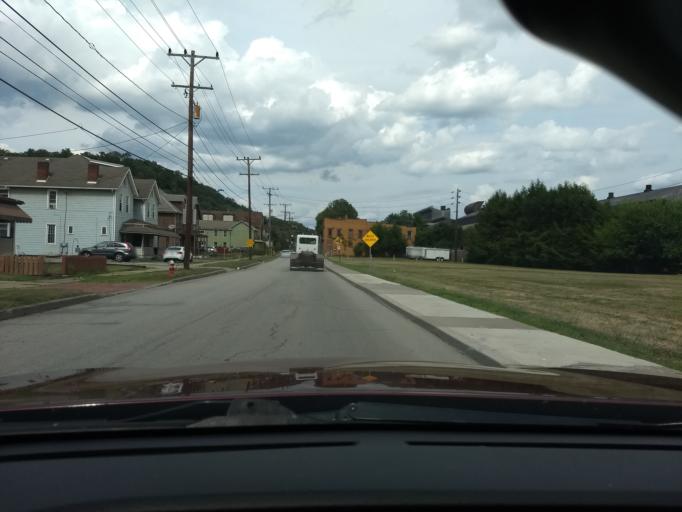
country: US
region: Pennsylvania
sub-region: Allegheny County
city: Brackenridge
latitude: 40.6171
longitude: -79.7224
